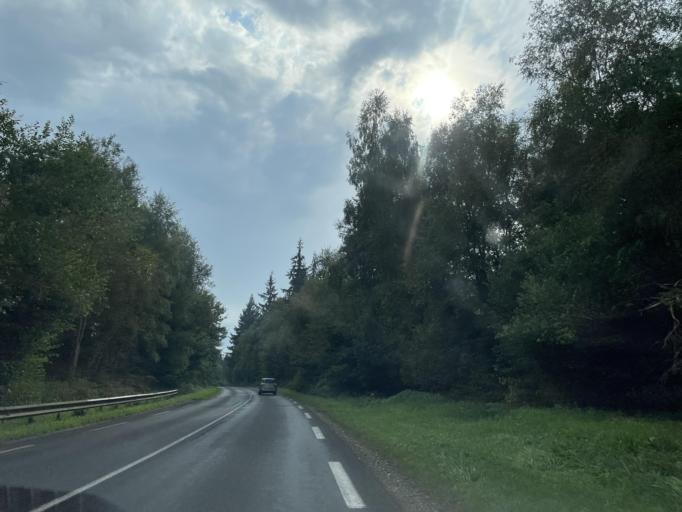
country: FR
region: Haute-Normandie
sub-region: Departement de la Seine-Maritime
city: Neufchatel-en-Bray
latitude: 49.7691
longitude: 1.4297
